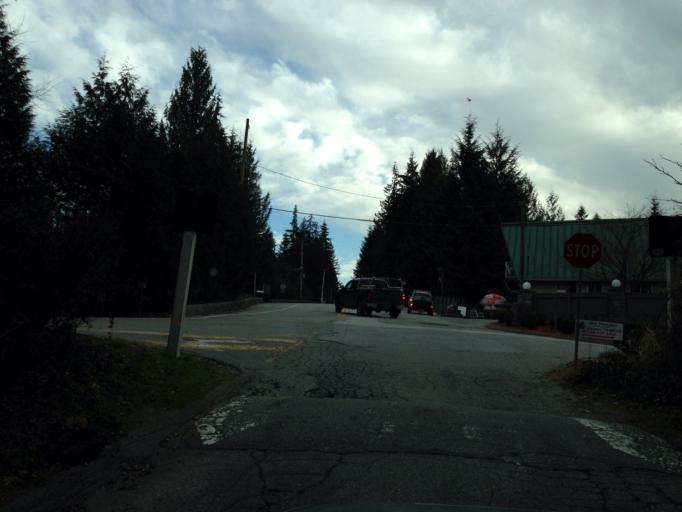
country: CA
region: British Columbia
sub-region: Greater Vancouver Regional District
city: Anmore
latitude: 49.3229
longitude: -122.8557
